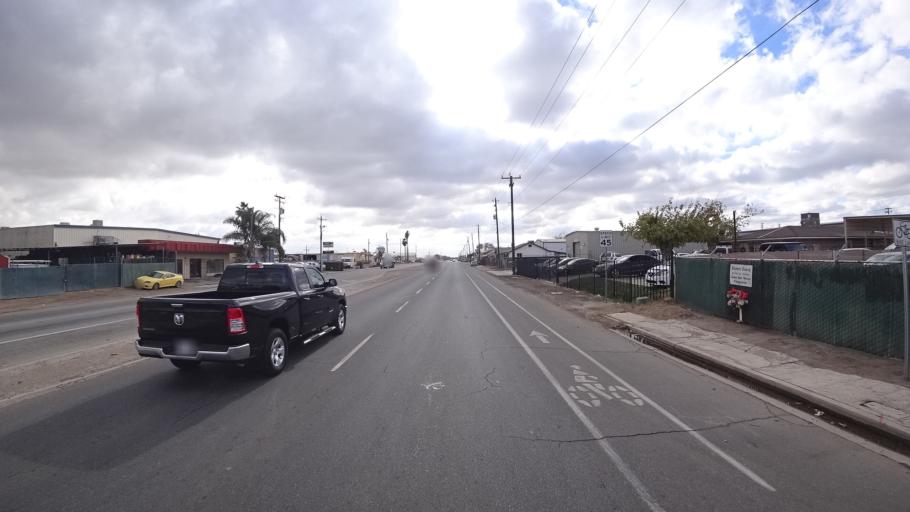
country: US
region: California
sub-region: Kern County
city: Bakersfield
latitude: 35.3613
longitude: -118.9676
